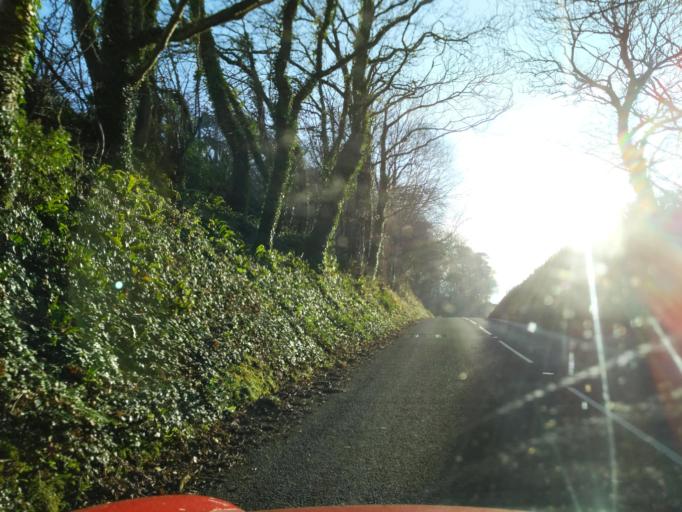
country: GB
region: England
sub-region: Cornwall
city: Pillaton
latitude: 50.4048
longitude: -4.3303
